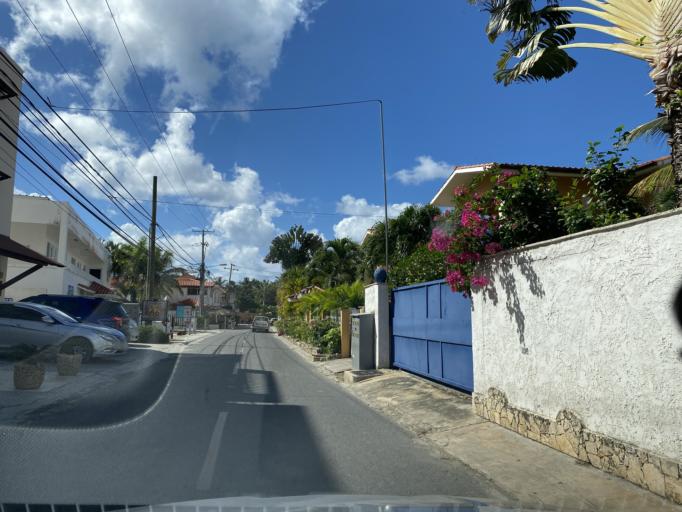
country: DO
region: La Romana
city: La Romana
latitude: 18.3487
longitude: -68.8255
